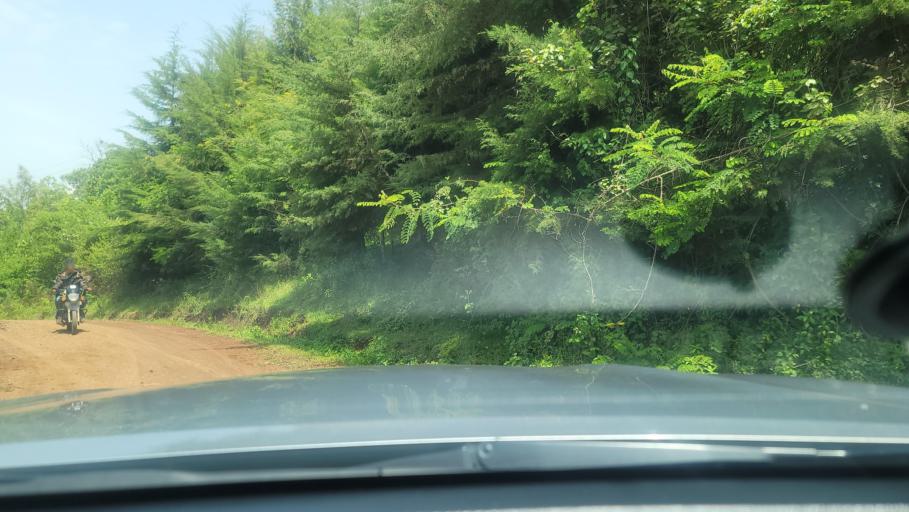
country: ET
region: Oromiya
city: Agaro
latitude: 7.8140
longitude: 36.4127
